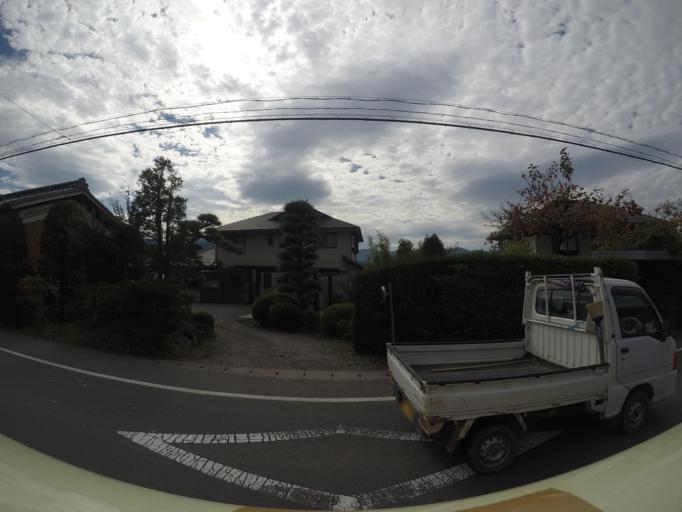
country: JP
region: Nagano
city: Ina
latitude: 35.8399
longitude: 138.0395
